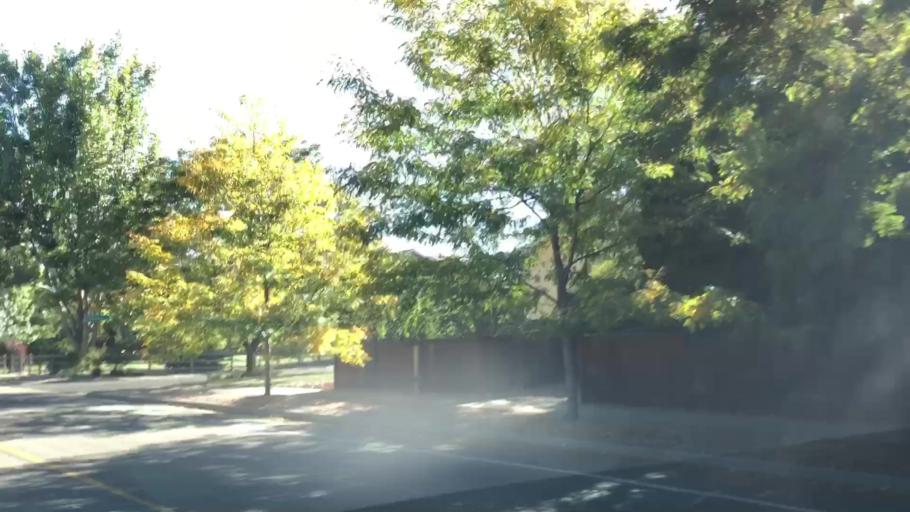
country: US
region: Colorado
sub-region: Larimer County
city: Loveland
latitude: 40.4906
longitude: -105.0618
